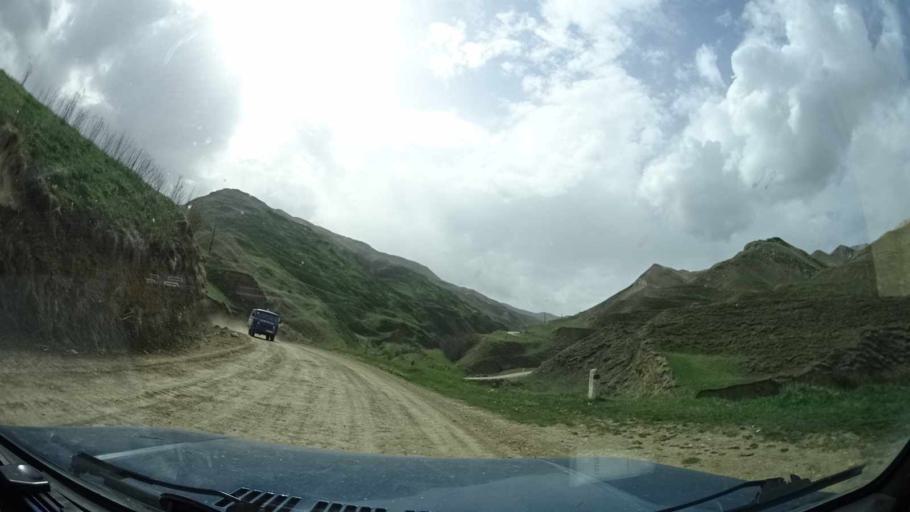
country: RU
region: Dagestan
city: Usisha
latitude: 42.1208
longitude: 47.3886
